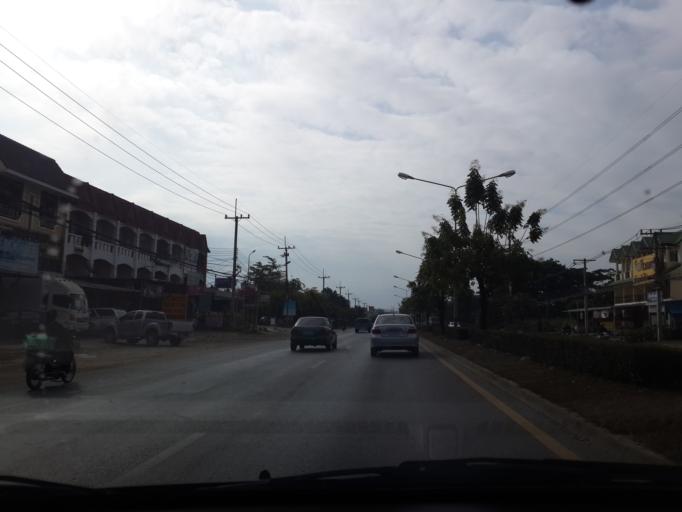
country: TH
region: Chiang Mai
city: San Sai
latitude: 18.8808
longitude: 99.0145
